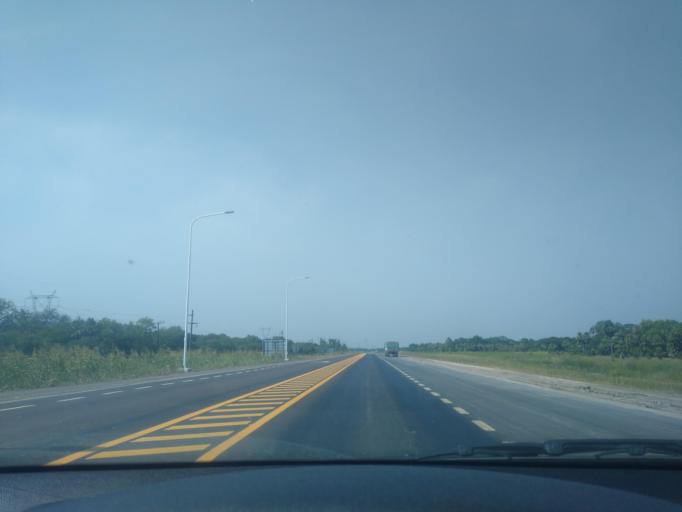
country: AR
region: Chaco
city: Fontana
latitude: -27.5758
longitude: -59.1571
